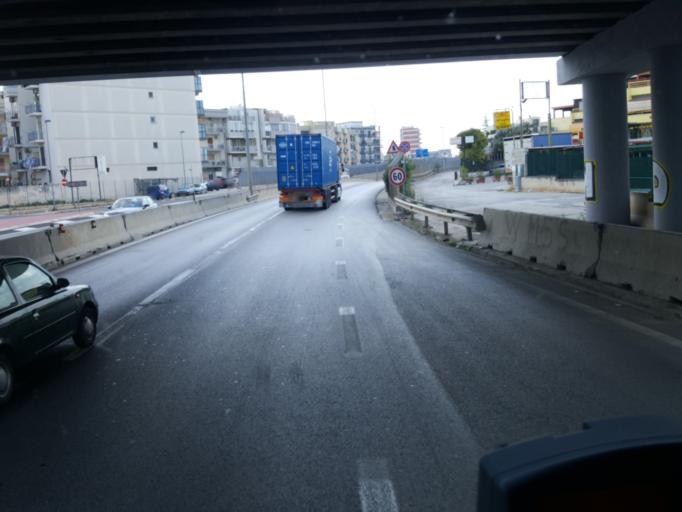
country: IT
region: Apulia
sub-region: Provincia di Bari
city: Modugno
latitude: 41.0896
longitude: 16.7809
